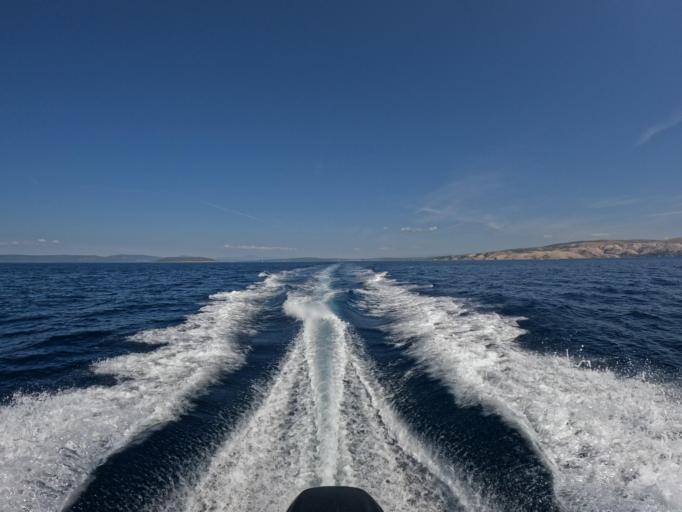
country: HR
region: Primorsko-Goranska
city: Punat
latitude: 44.9107
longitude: 14.6281
